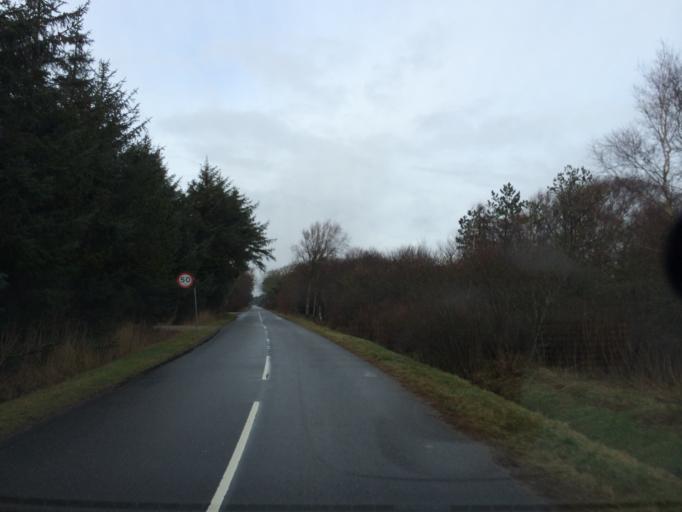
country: DK
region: Central Jutland
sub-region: Holstebro Kommune
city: Ulfborg
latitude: 56.2626
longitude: 8.1510
